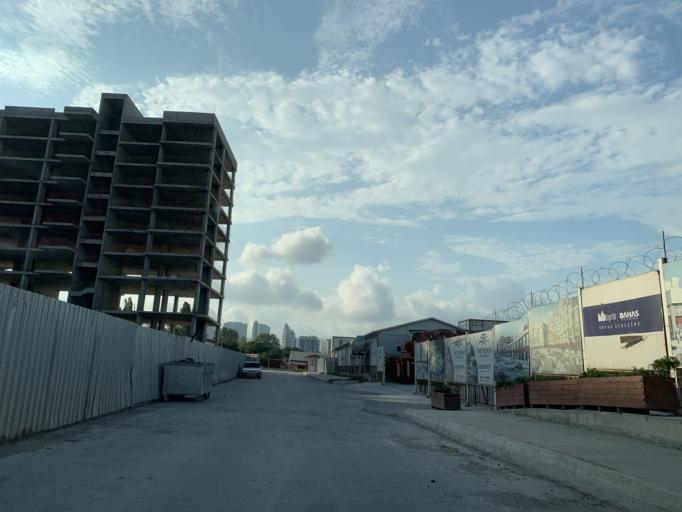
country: TR
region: Istanbul
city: Esenyurt
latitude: 41.0467
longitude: 28.6774
